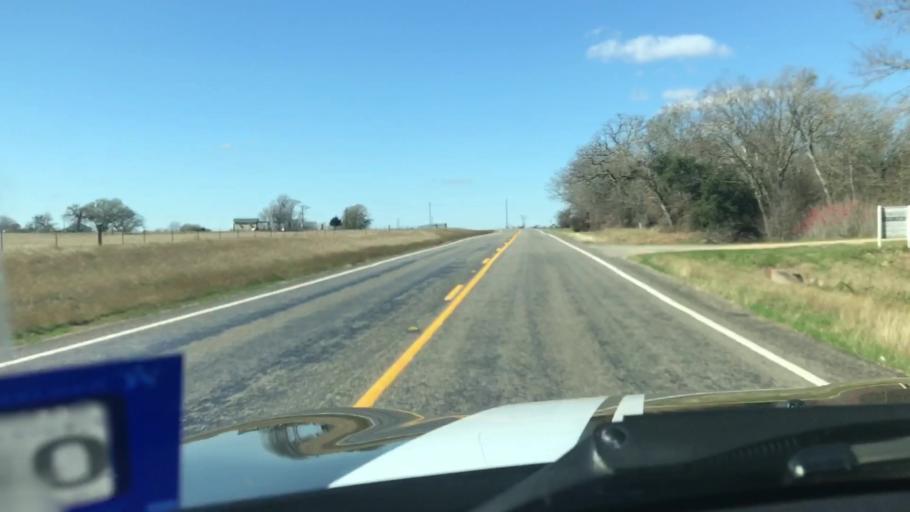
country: US
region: Texas
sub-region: Robertson County
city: Calvert
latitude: 30.8839
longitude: -96.7497
